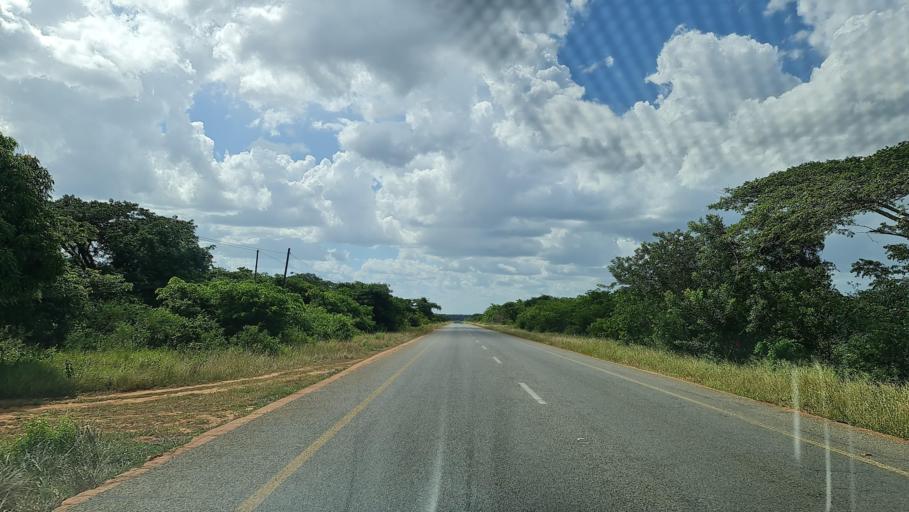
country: MZ
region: Inhambane
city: Maxixe
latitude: -22.9721
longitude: 35.2182
